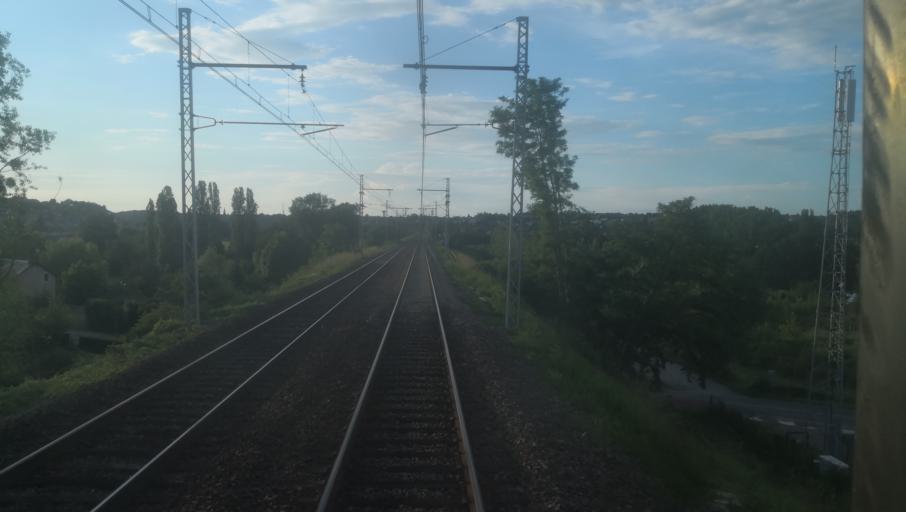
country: FR
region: Centre
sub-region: Departement de l'Indre
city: Argenton-sur-Creuse
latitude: 46.5763
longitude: 1.5269
